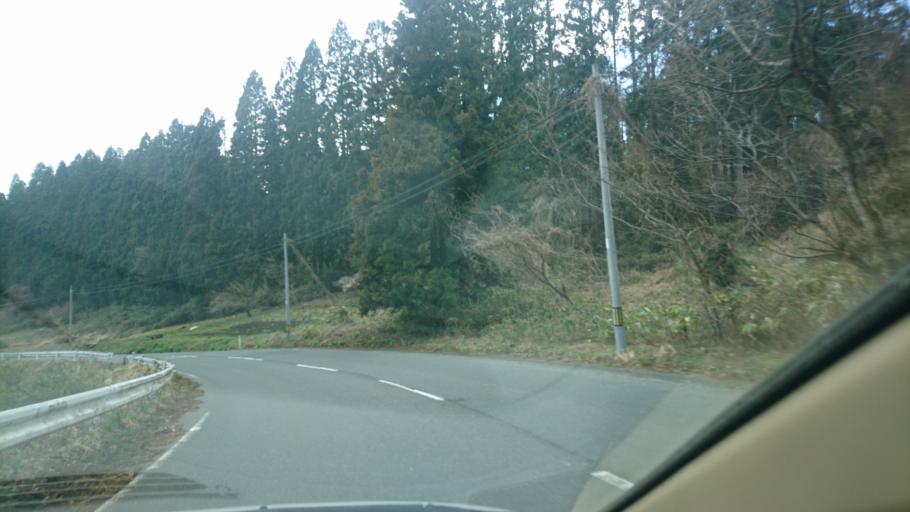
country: JP
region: Miyagi
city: Furukawa
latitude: 38.7206
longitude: 140.8325
